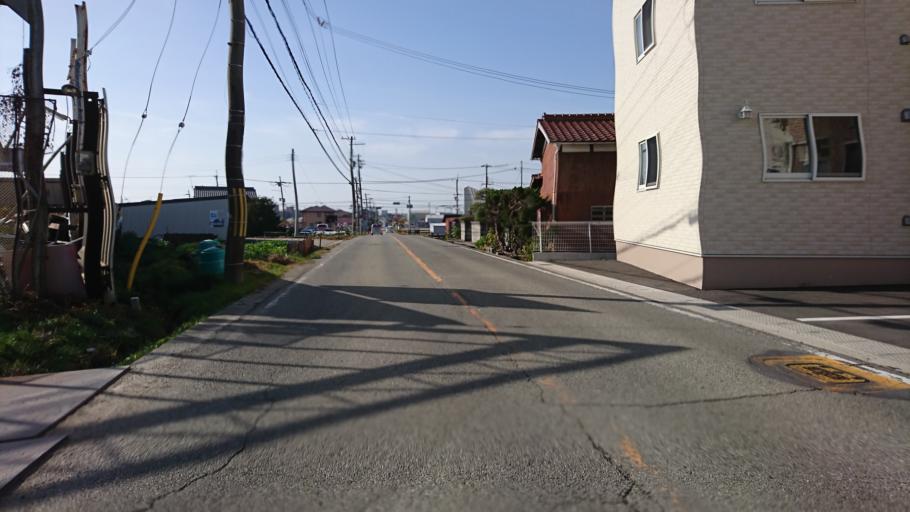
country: JP
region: Hyogo
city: Kakogawacho-honmachi
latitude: 34.7315
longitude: 134.8733
